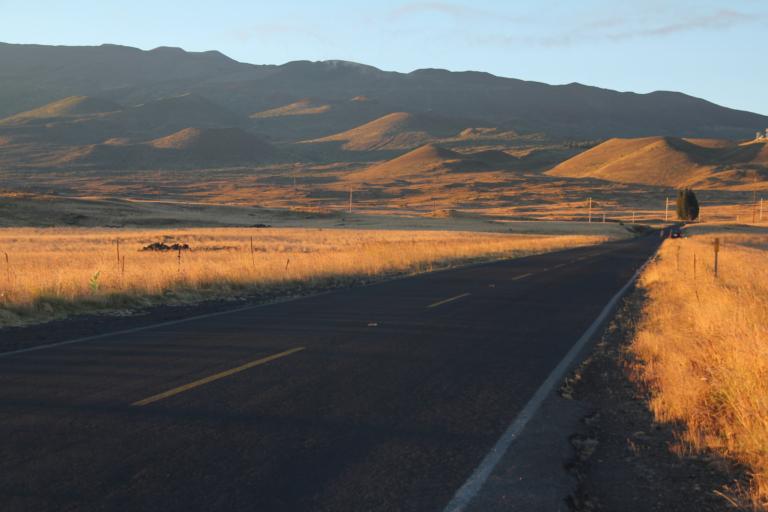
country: US
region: Hawaii
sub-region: Hawaii County
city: Volcano
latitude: 19.6931
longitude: -155.4652
